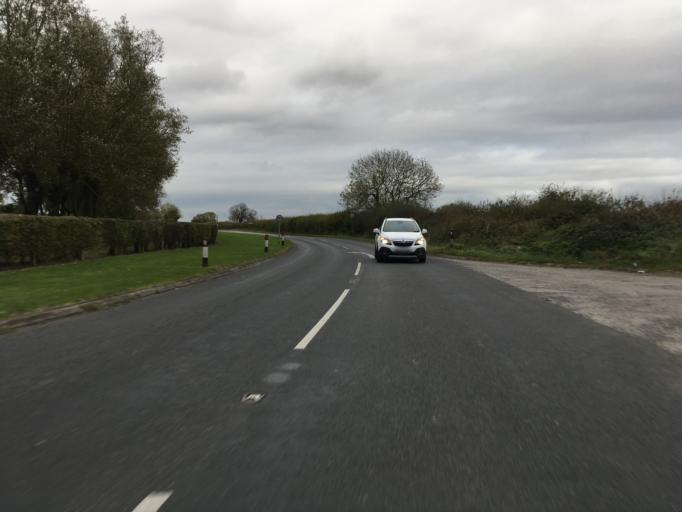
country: GB
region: England
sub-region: South Gloucestershire
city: Pucklechurch
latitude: 51.5032
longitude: -2.4282
